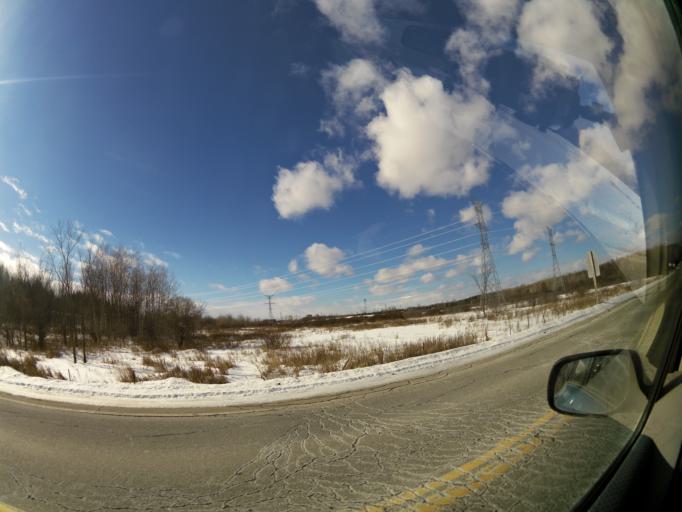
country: CA
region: Ontario
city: Ottawa
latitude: 45.3970
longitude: -75.5824
